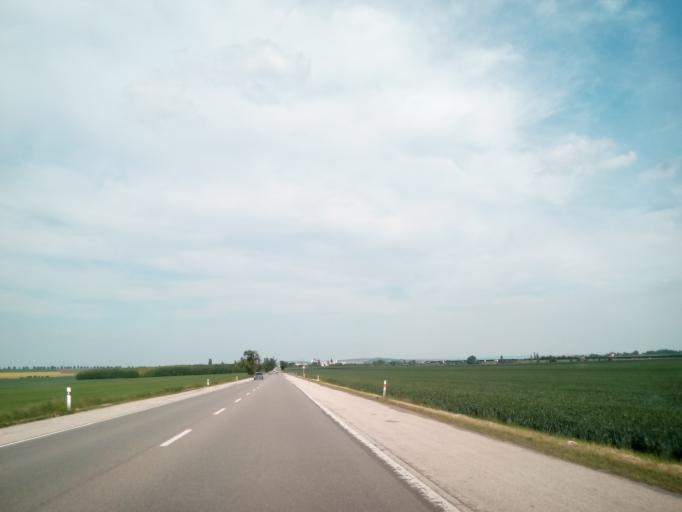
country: CZ
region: South Moravian
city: Tvarozna
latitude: 49.1850
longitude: 16.7838
